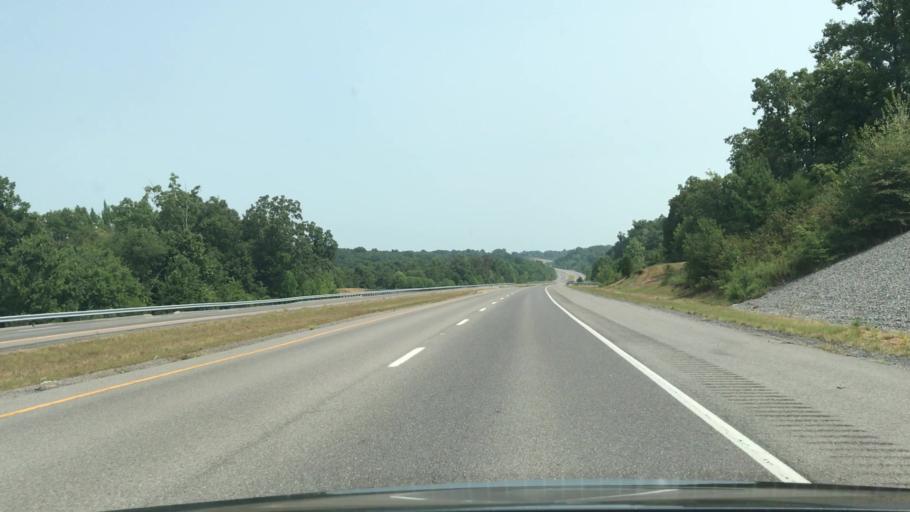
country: US
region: Kentucky
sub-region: Calloway County
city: Murray
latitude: 36.7487
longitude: -88.1588
